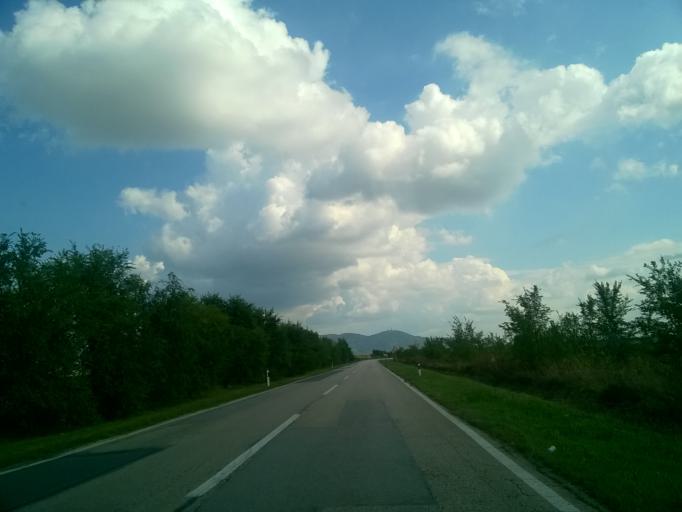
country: RS
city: Pavlis
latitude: 45.1552
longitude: 21.2515
